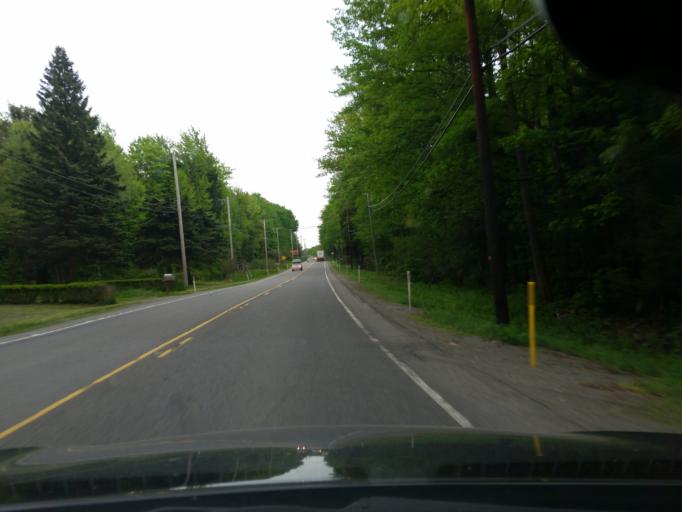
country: US
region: Pennsylvania
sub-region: Elk County
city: Ridgway
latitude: 41.3935
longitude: -78.6928
